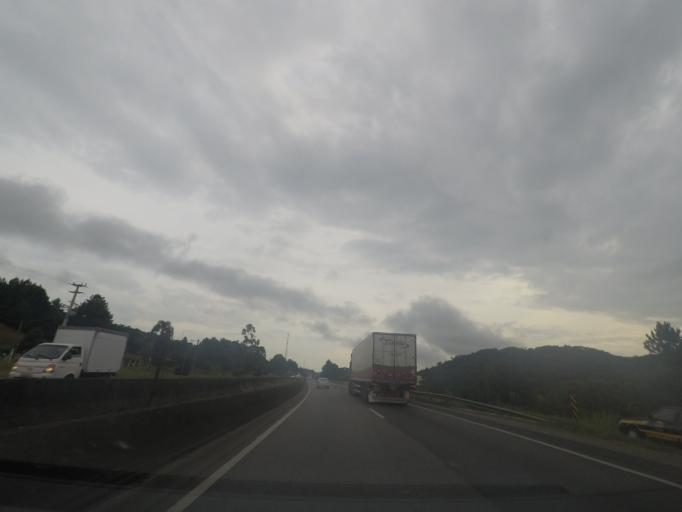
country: BR
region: Parana
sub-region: Campina Grande Do Sul
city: Campina Grande do Sul
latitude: -25.3206
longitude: -49.0228
